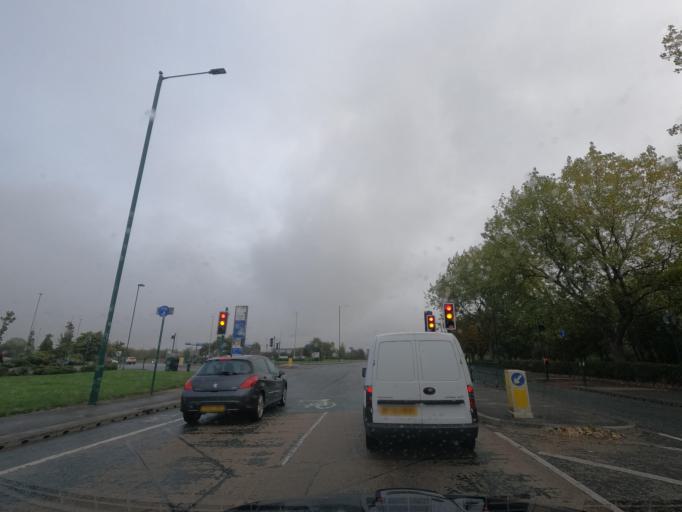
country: GB
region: England
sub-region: Redcar and Cleveland
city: South Bank
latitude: 54.5714
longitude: -1.1630
